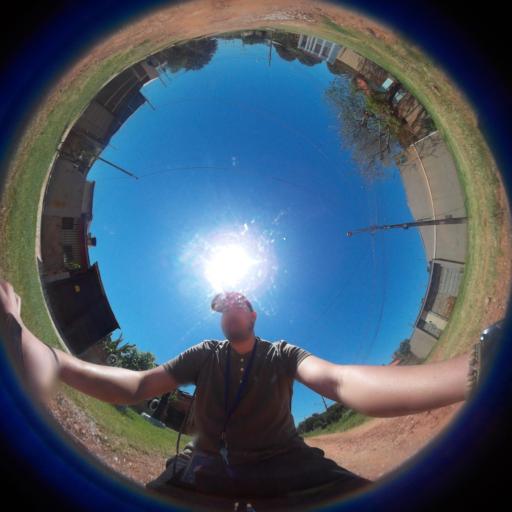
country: BR
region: Mato Grosso do Sul
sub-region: Ponta Pora
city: Ponta Pora
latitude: -22.5255
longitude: -55.7324
